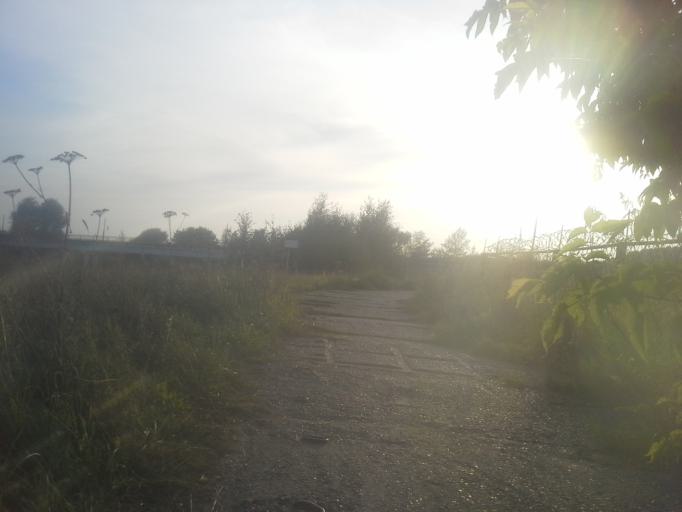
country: RU
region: Moskovskaya
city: Nikolina Gora
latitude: 55.7278
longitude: 37.0902
